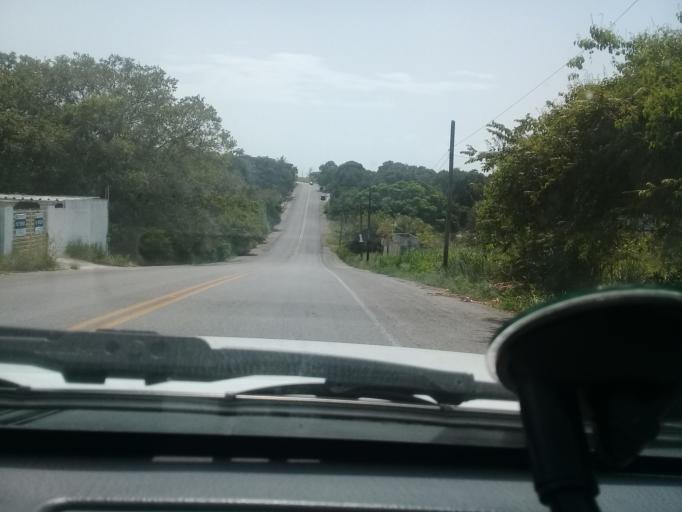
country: MX
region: Veracruz
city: Villa Cuauhtemoc
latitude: 22.2126
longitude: -97.8253
